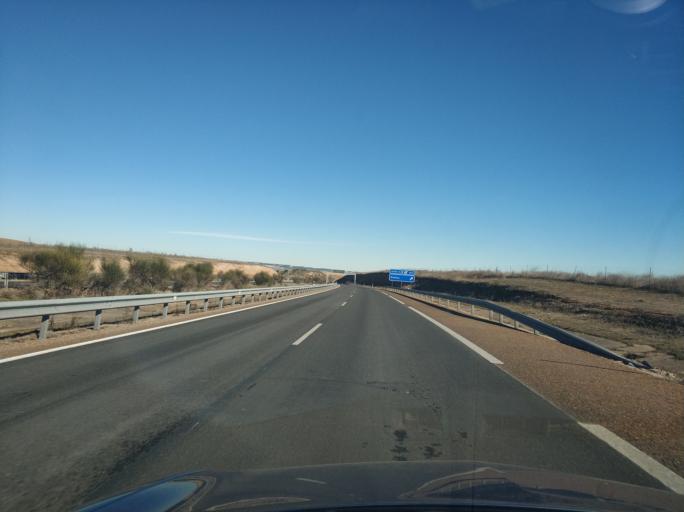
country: ES
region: Castille and Leon
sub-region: Provincia de Valladolid
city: Pollos
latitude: 41.4388
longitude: -5.0934
